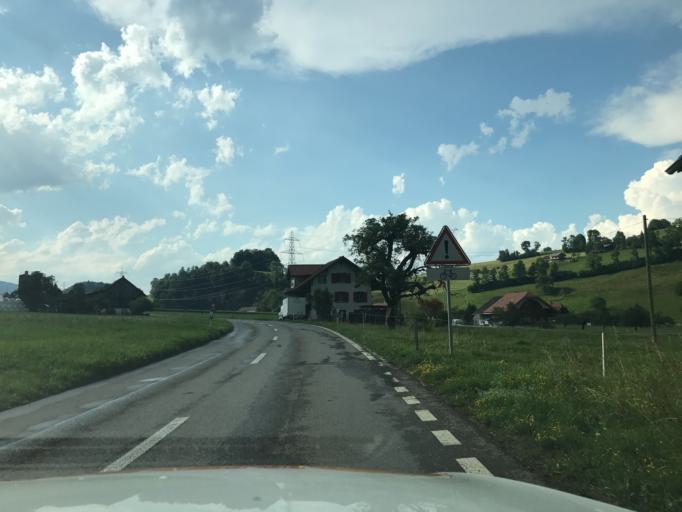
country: CH
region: Bern
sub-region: Thun District
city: Thierachern
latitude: 46.7113
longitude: 7.5725
